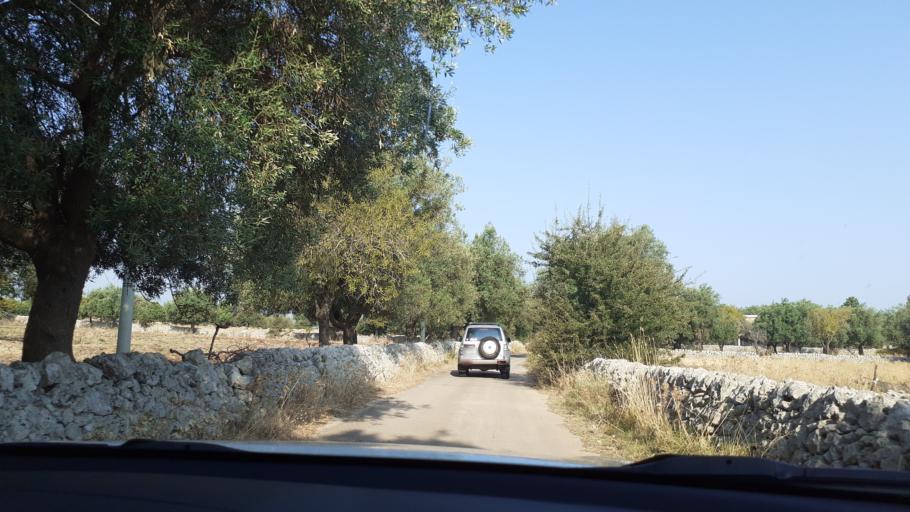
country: IT
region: Sicily
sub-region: Provincia di Siracusa
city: Cassibile
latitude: 36.9798
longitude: 15.1464
